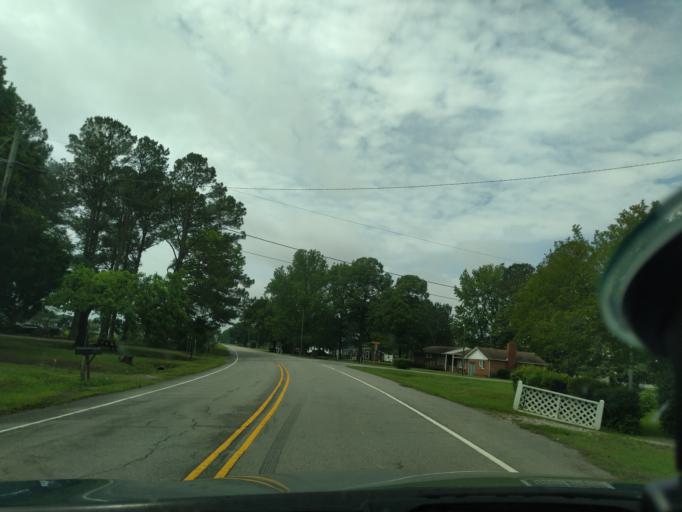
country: US
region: North Carolina
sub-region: Chowan County
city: Edenton
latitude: 35.9190
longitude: -76.5990
